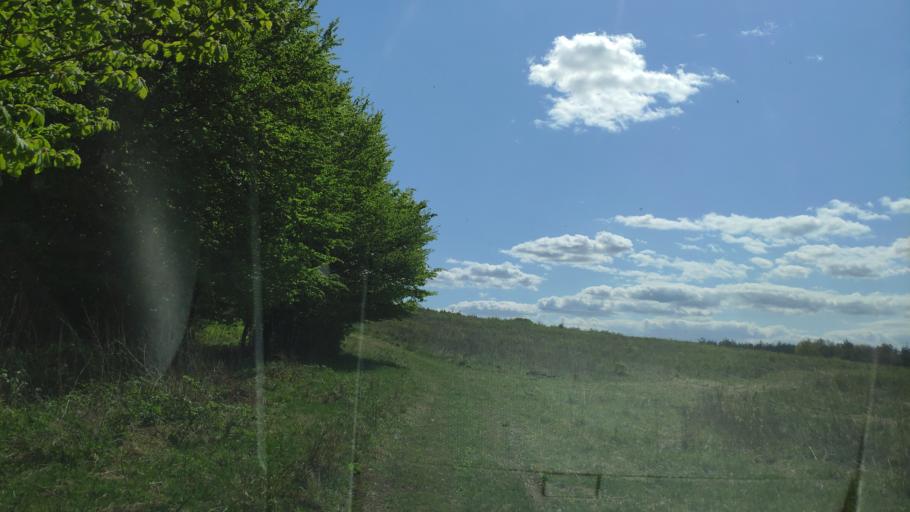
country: SK
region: Kosicky
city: Kosice
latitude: 48.6693
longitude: 21.4302
